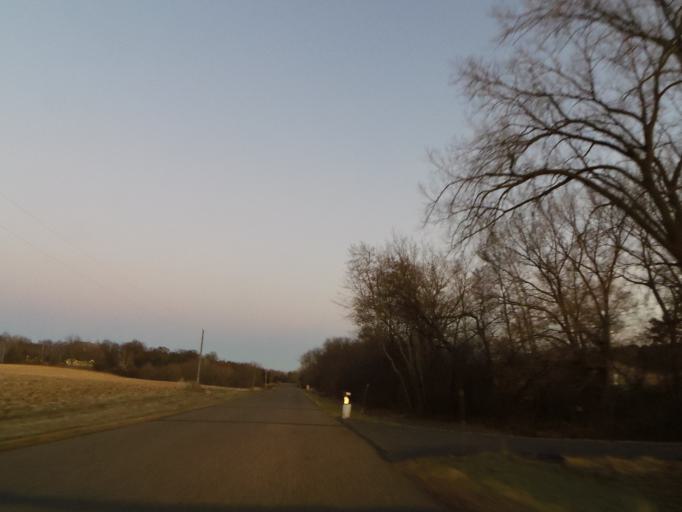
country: US
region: Wisconsin
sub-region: Pierce County
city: River Falls
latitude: 44.9313
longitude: -92.6737
